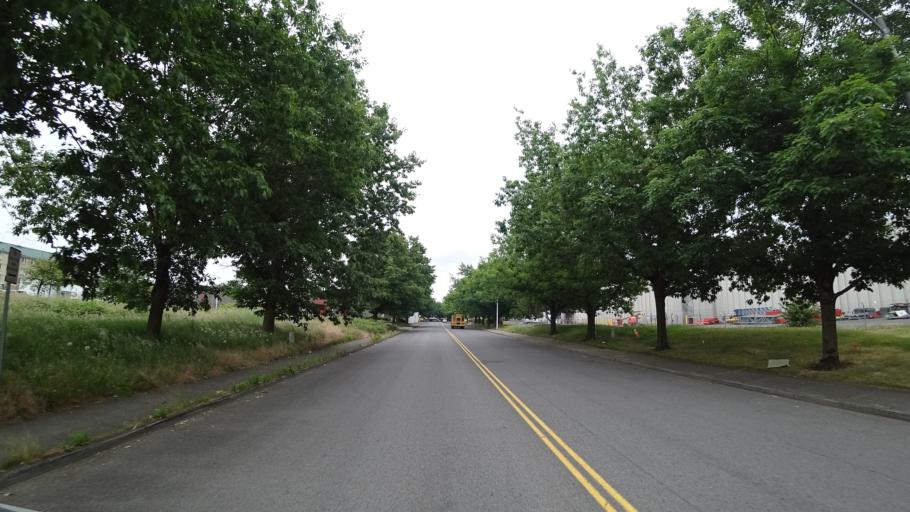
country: US
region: Oregon
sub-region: Multnomah County
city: Fairview
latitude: 45.5391
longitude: -122.4800
